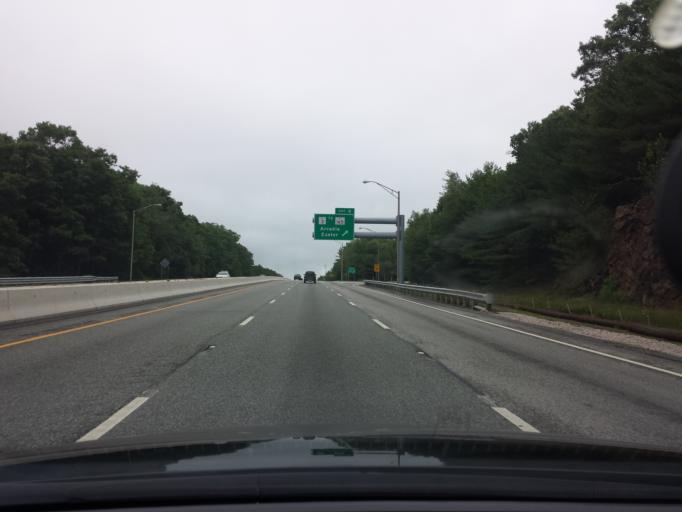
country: US
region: Rhode Island
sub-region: Washington County
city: Hope Valley
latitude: 41.5349
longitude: -71.6800
